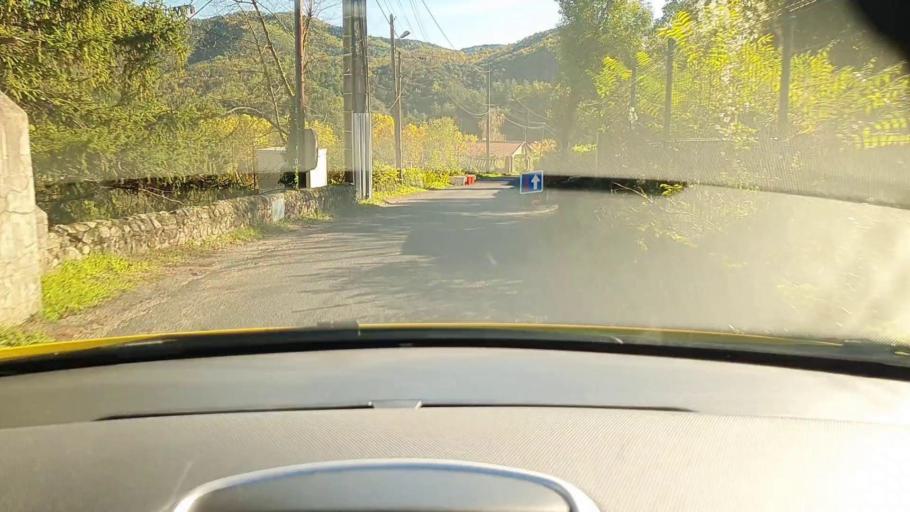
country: FR
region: Languedoc-Roussillon
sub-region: Departement du Gard
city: Le Vigan
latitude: 43.9937
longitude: 3.6212
